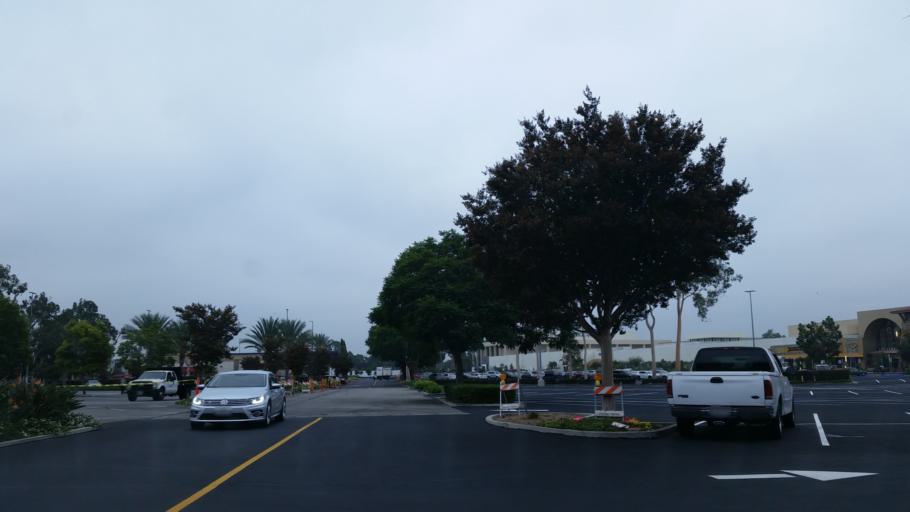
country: US
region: California
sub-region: Los Angeles County
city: Artesia
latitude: 33.8639
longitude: -118.0920
